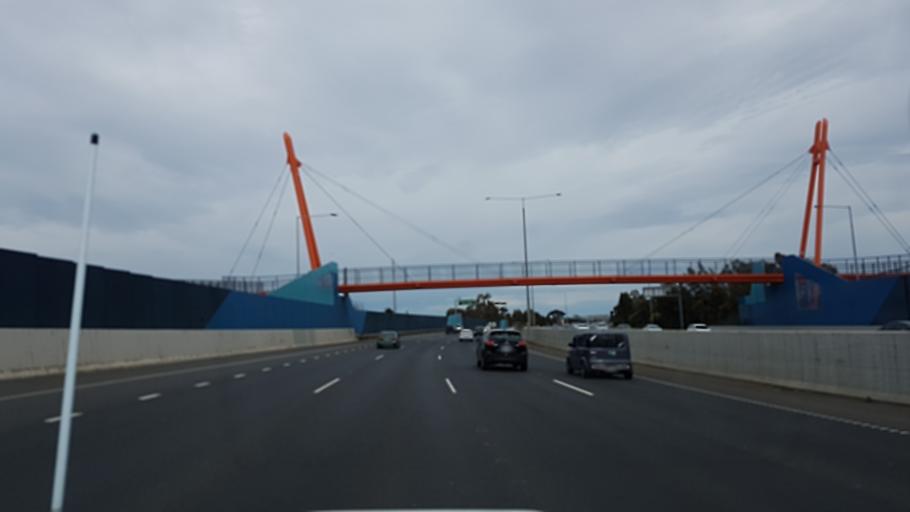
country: AU
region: Victoria
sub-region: Hobsons Bay
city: Laverton
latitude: -37.8675
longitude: 144.7722
